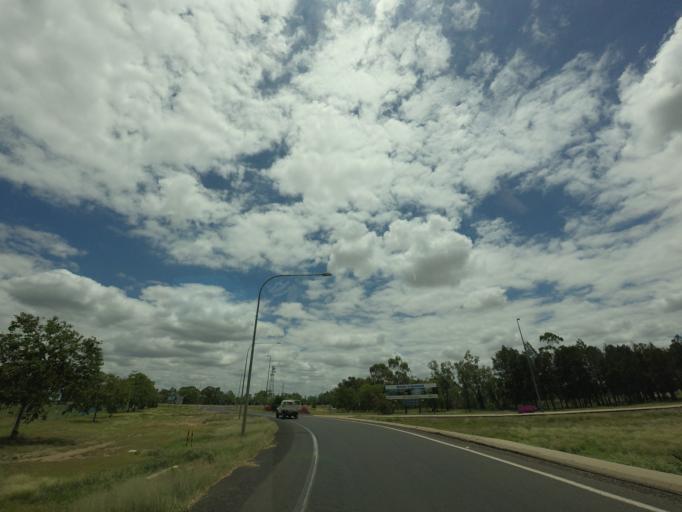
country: AU
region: Queensland
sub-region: Goondiwindi
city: Goondiwindi
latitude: -28.5524
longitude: 150.3225
